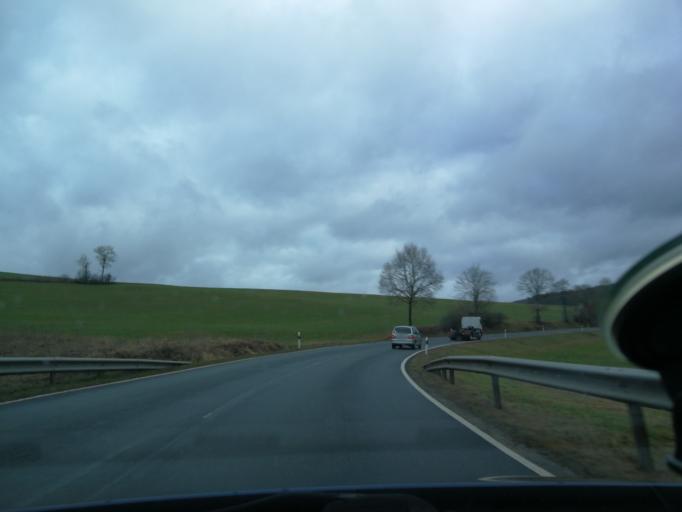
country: DE
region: Rheinland-Pfalz
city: Oberehe-Stroheich
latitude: 50.2700
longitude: 6.7728
